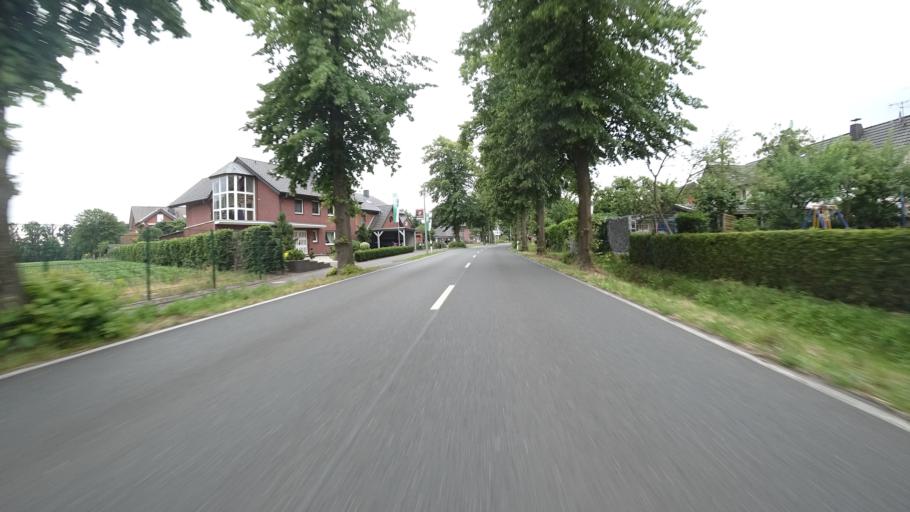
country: DE
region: North Rhine-Westphalia
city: Rietberg
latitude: 51.8292
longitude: 8.4035
